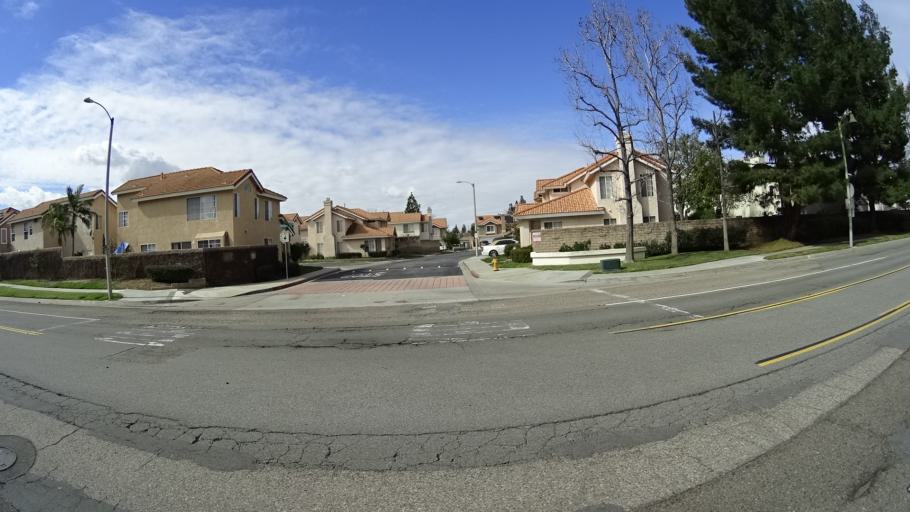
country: US
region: California
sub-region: Orange County
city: Yorba Linda
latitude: 33.8689
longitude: -117.8259
